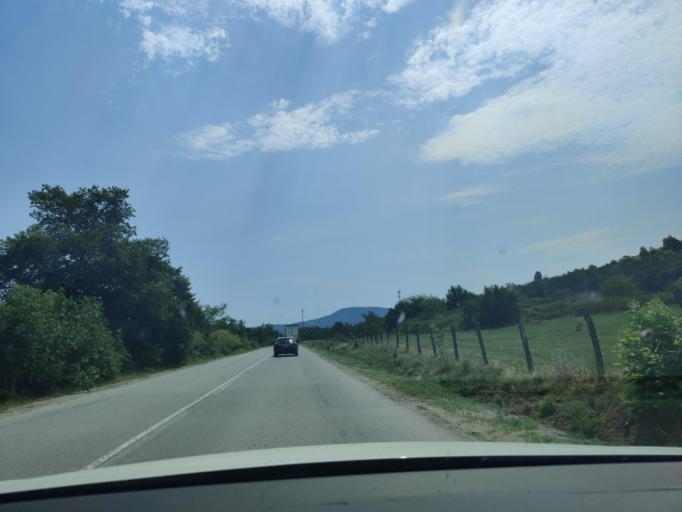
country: BG
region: Montana
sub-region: Obshtina Chiprovtsi
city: Chiprovtsi
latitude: 43.5074
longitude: 22.9828
